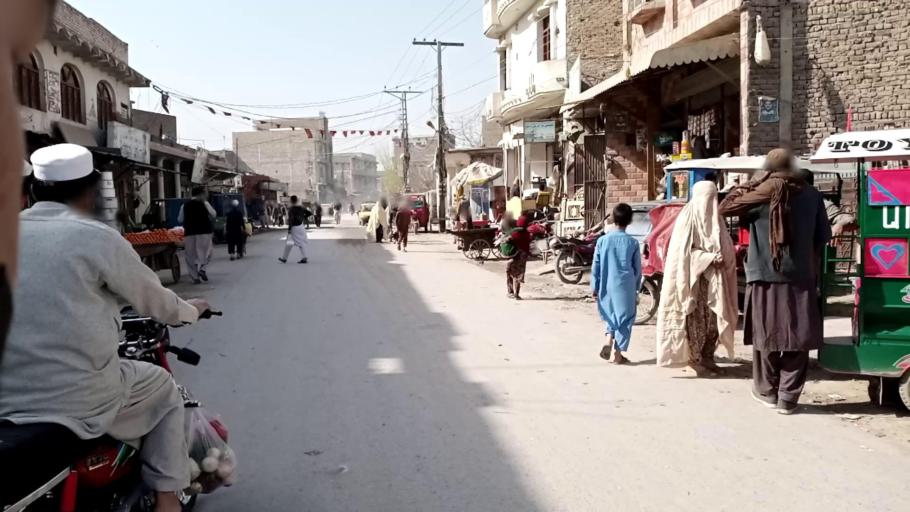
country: PK
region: Khyber Pakhtunkhwa
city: Peshawar
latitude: 33.9920
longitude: 71.5834
